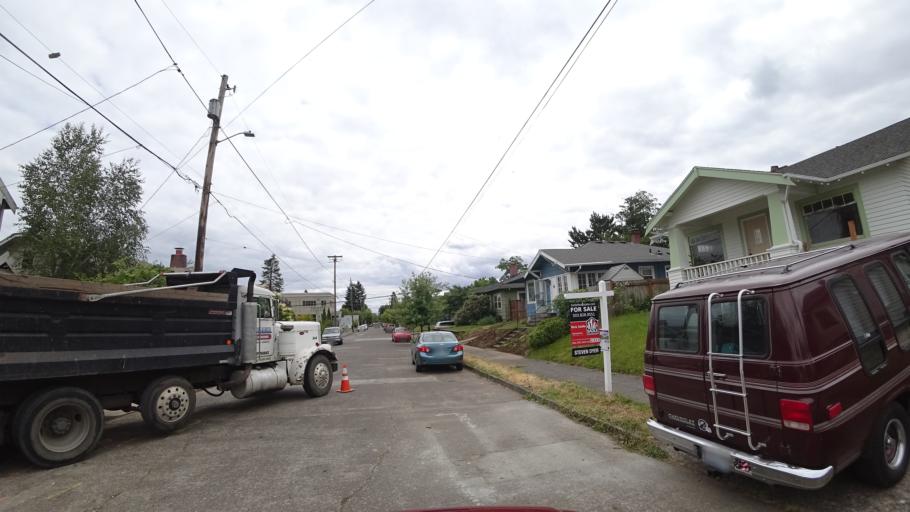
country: US
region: Oregon
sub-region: Multnomah County
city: Portland
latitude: 45.5765
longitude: -122.6771
